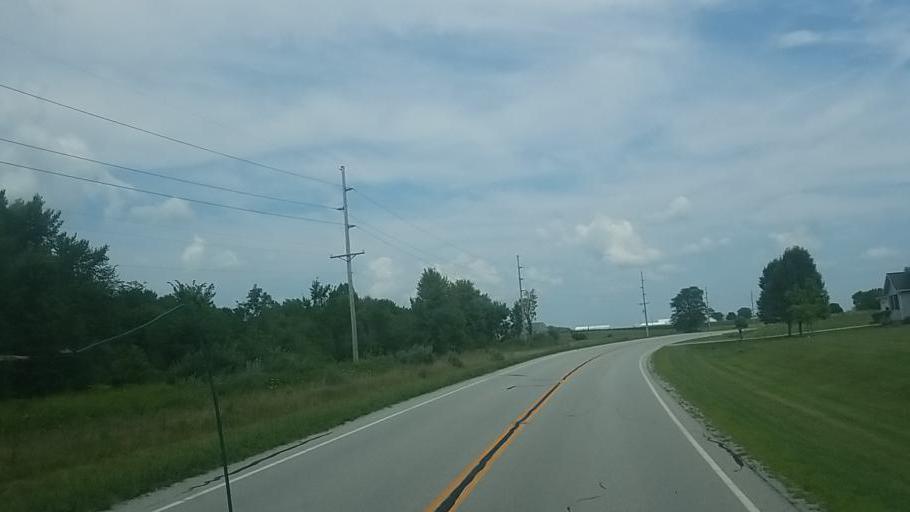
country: US
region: Ohio
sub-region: Hardin County
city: Forest
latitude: 40.7824
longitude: -83.5714
